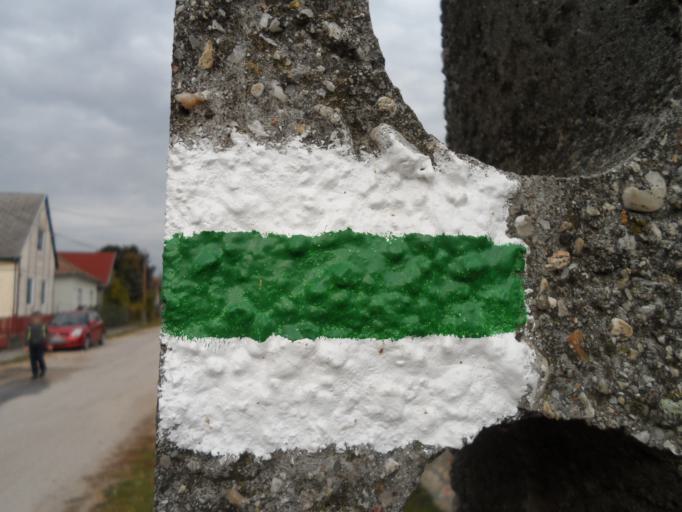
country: HU
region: Fejer
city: Kincsesbanya
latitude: 47.2408
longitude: 18.3386
